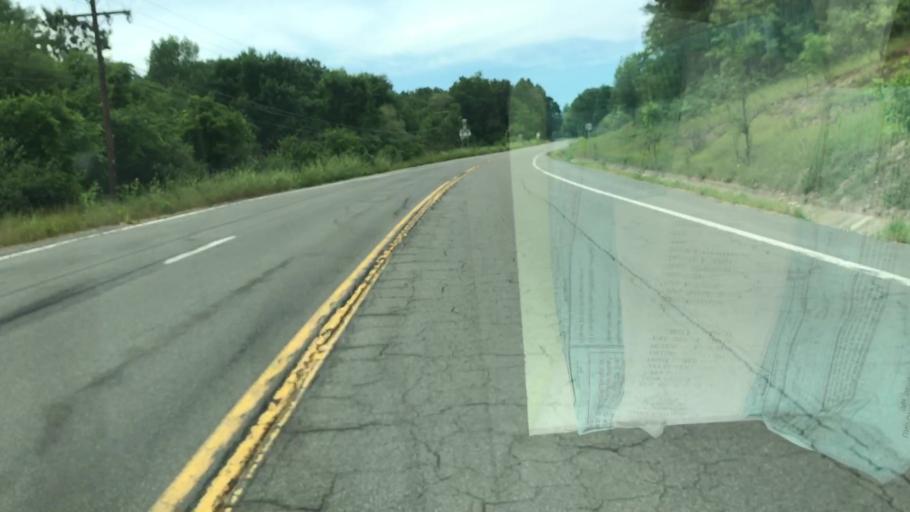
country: US
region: New York
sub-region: Onondaga County
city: Marcellus
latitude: 42.9312
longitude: -76.3363
